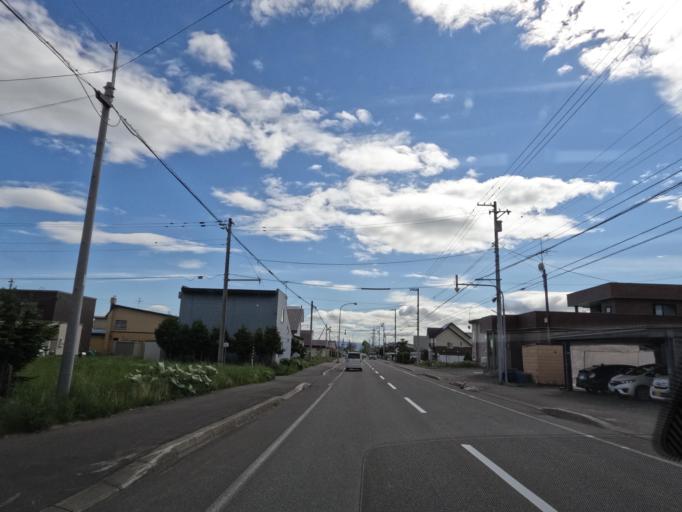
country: JP
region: Hokkaido
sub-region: Asahikawa-shi
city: Asahikawa
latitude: 43.8270
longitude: 142.5236
